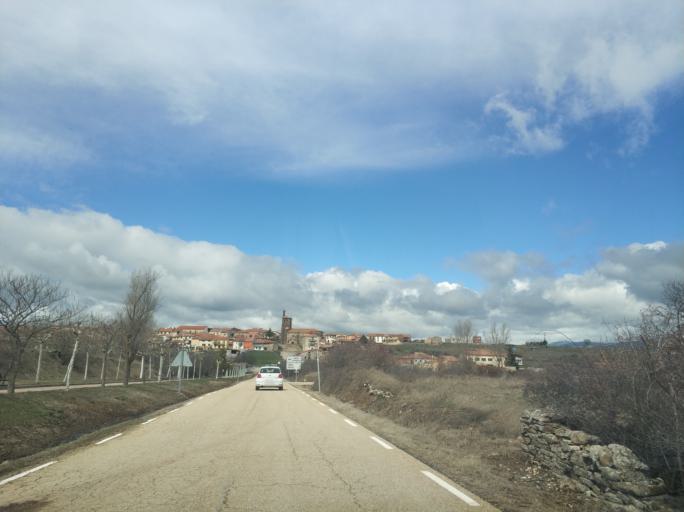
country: ES
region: Castille and Leon
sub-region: Provincia de Soria
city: Abejar
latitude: 41.8044
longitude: -2.7812
